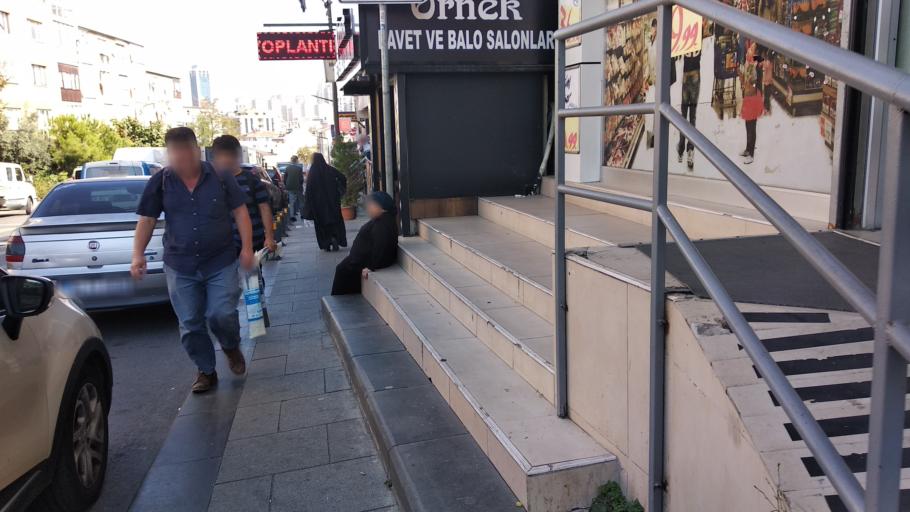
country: TR
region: Istanbul
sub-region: Atasehir
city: Atasehir
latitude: 40.9955
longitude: 29.0832
